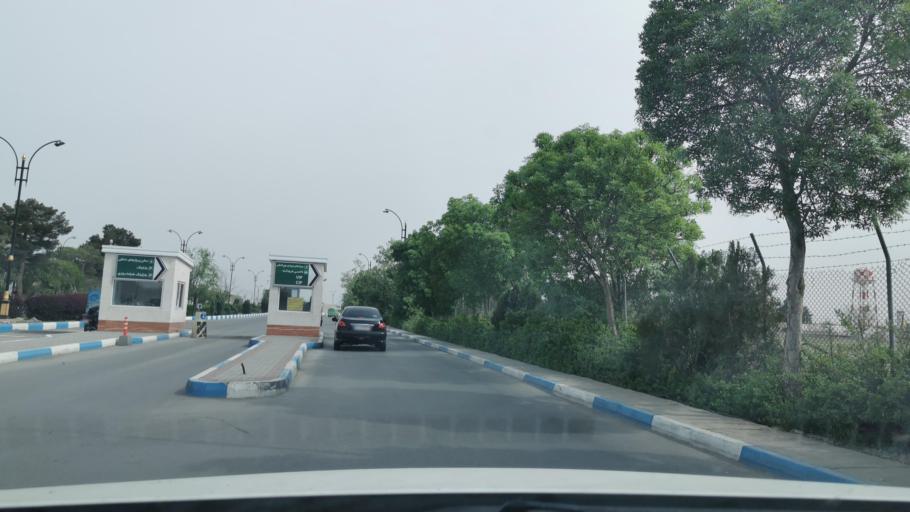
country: IR
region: Razavi Khorasan
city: Mashhad
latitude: 36.2298
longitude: 59.6374
